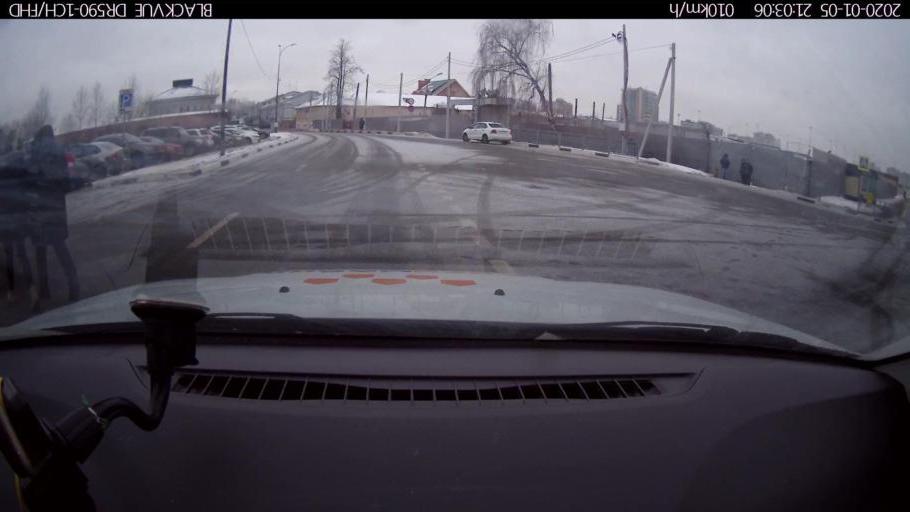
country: RU
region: Nizjnij Novgorod
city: Nizhniy Novgorod
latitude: 56.3328
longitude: 43.9708
